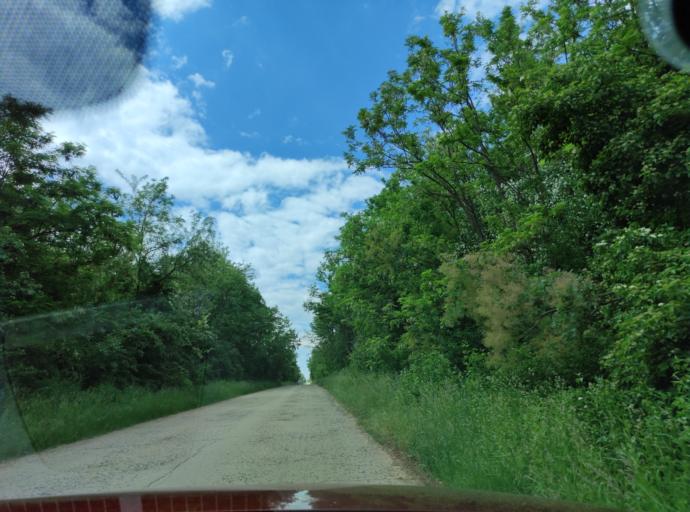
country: BG
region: Montana
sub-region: Obshtina Berkovitsa
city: Berkovitsa
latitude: 43.3590
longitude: 23.0922
